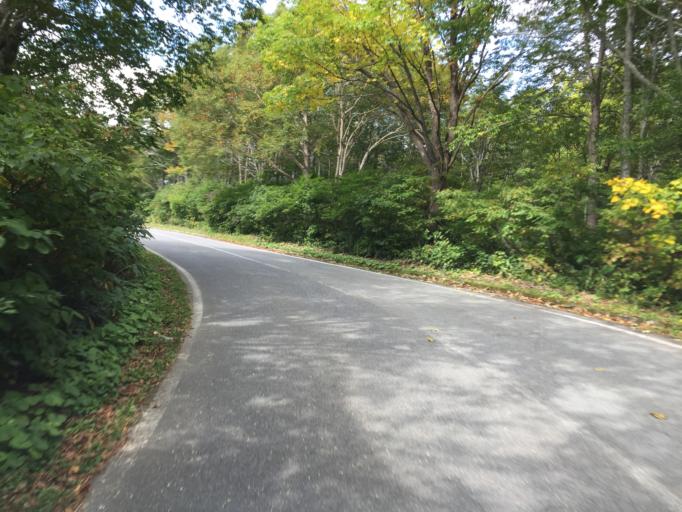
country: JP
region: Fukushima
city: Inawashiro
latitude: 37.6139
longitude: 140.0488
